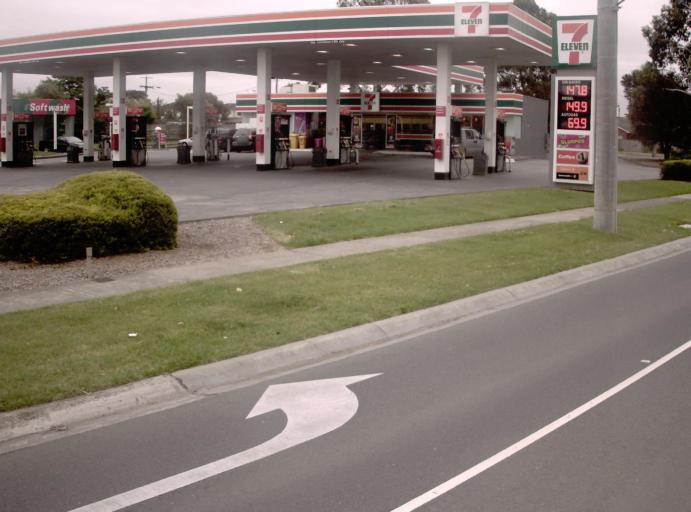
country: AU
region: Victoria
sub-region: Casey
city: Hallam
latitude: -38.0025
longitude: 145.2740
